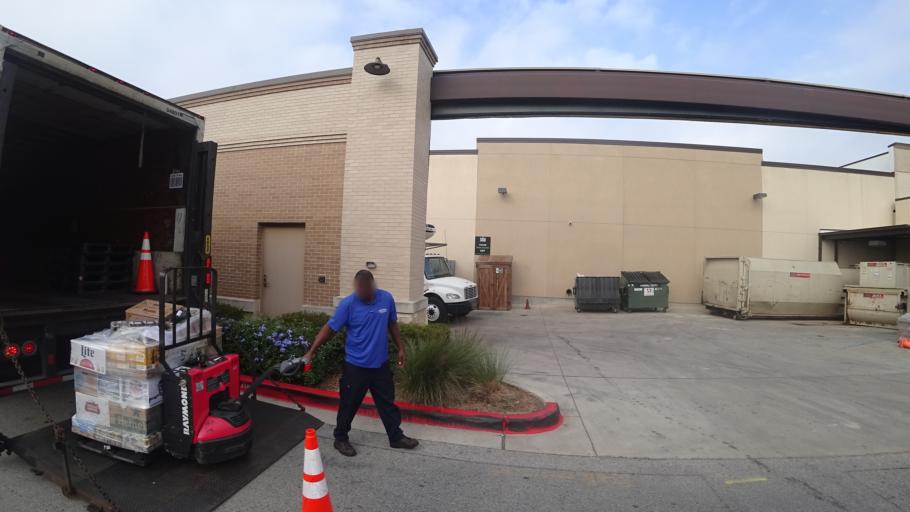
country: US
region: Texas
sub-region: Travis County
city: Bee Cave
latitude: 30.3074
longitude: -97.9372
